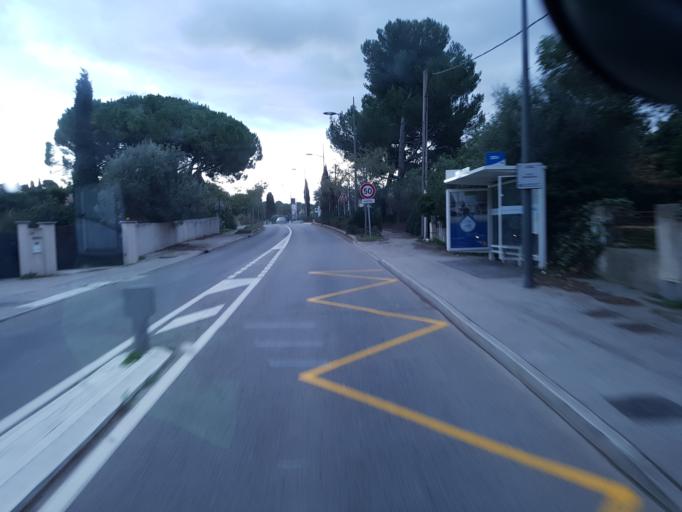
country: FR
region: Provence-Alpes-Cote d'Azur
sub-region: Departement du Var
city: Sanary-sur-Mer
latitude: 43.1283
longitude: 5.7844
